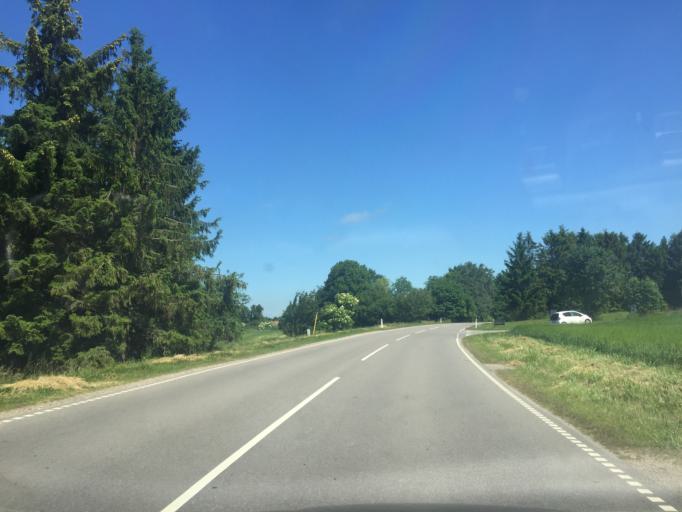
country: DK
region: Capital Region
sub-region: Hoje-Taastrup Kommune
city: Flong
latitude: 55.6592
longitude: 12.1979
